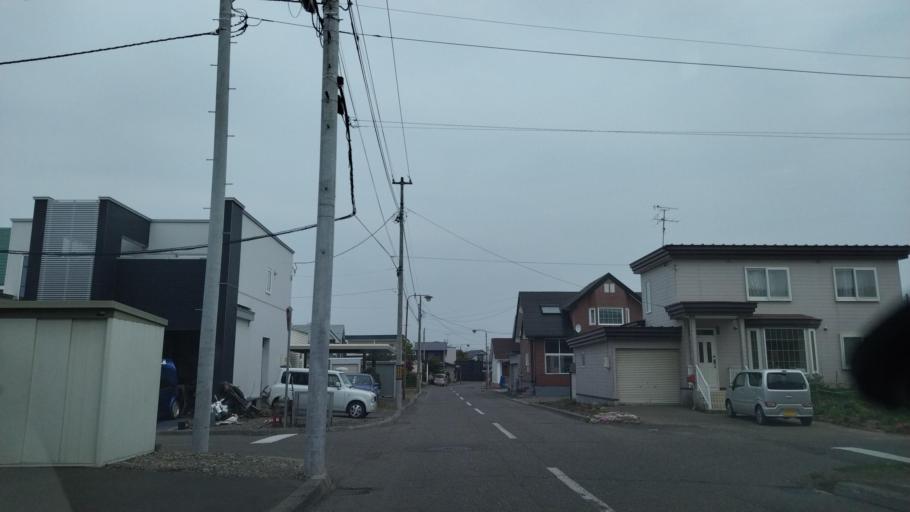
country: JP
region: Hokkaido
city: Obihiro
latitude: 42.9132
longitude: 143.0608
